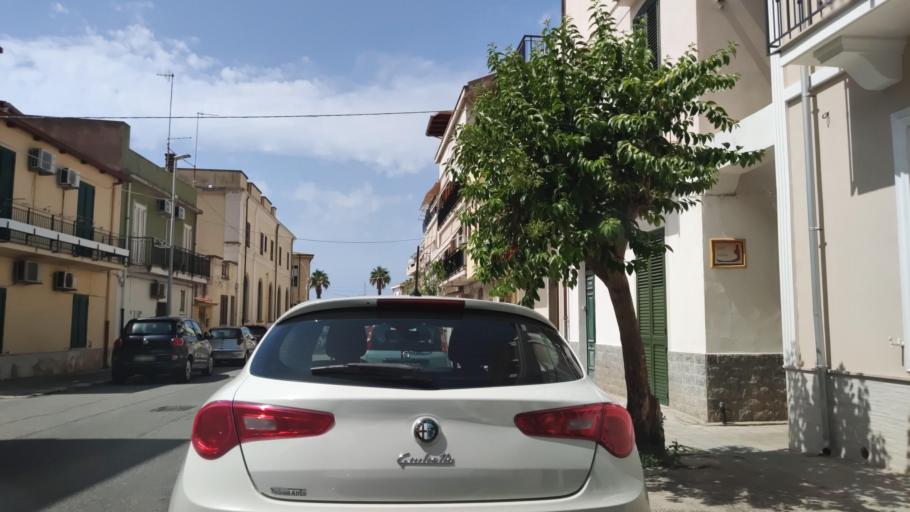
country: IT
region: Calabria
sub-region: Provincia di Reggio Calabria
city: Bagnara Calabra
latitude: 38.2843
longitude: 15.8014
